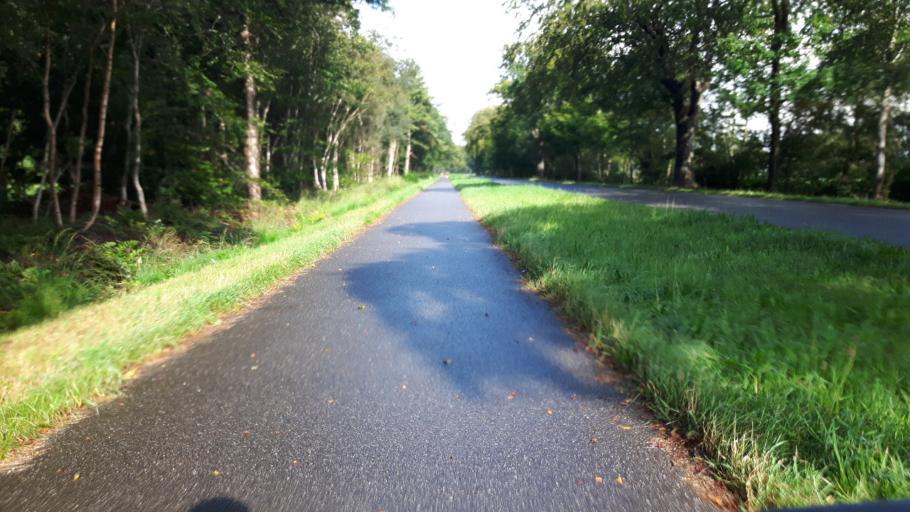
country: NL
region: Friesland
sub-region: Gemeente Smallingerland
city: Drachten
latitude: 53.0711
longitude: 6.1021
